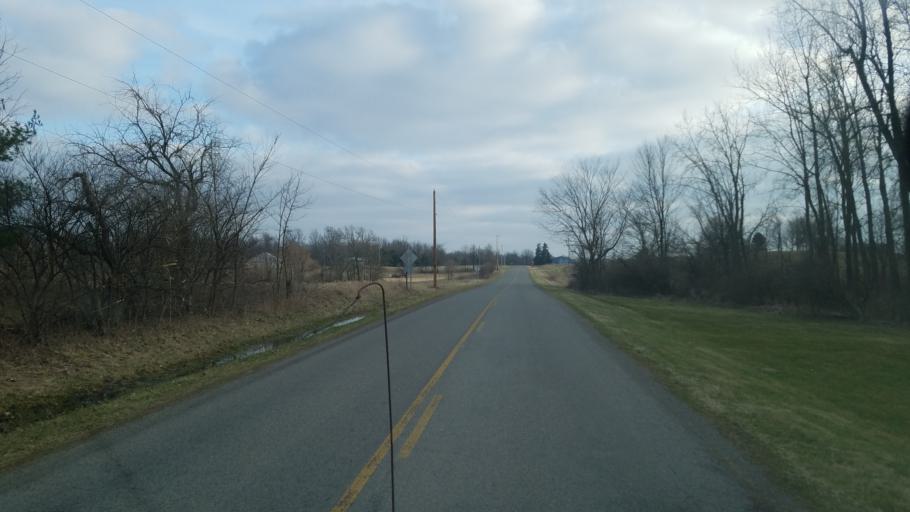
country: US
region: Ohio
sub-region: Logan County
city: Bellefontaine
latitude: 40.3159
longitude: -83.6640
